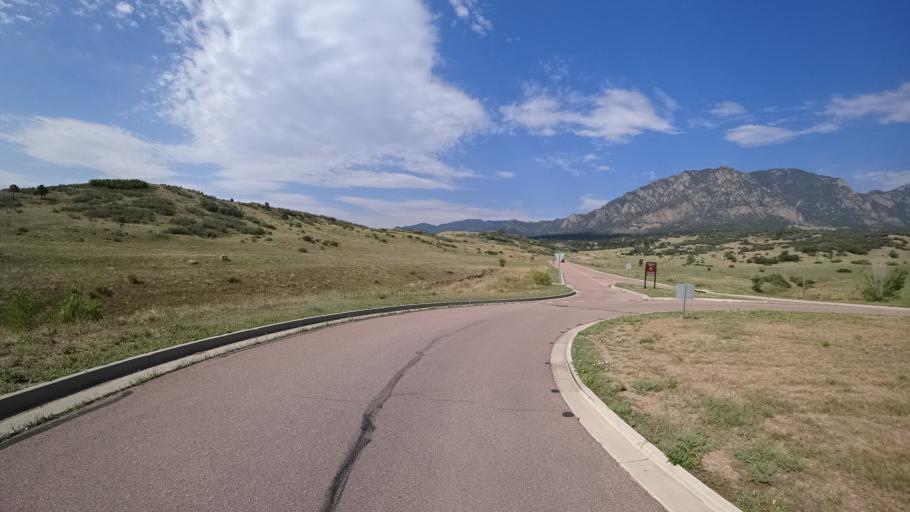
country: US
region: Colorado
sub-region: El Paso County
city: Fort Carson
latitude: 38.7377
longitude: -104.8114
